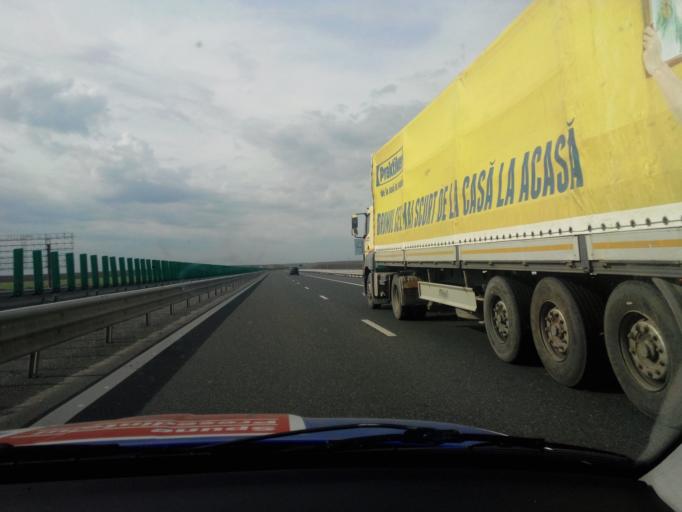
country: RO
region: Constanta
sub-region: Comuna Cumpana
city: Cumpana
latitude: 44.1438
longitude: 28.5368
